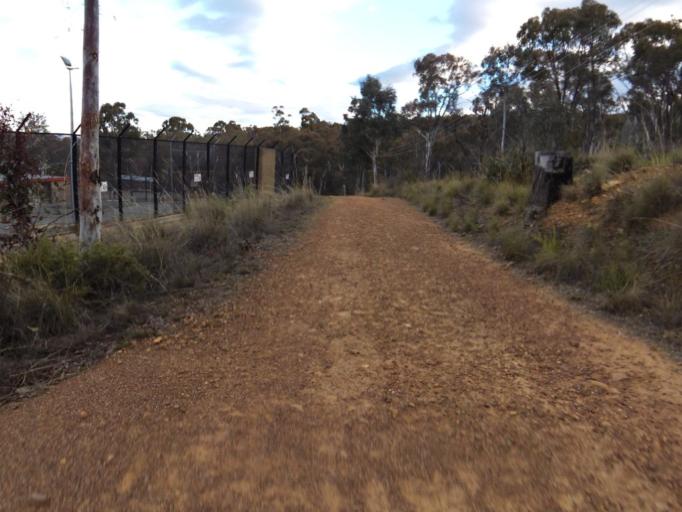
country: AU
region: Australian Capital Territory
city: Acton
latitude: -35.2693
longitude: 149.1084
